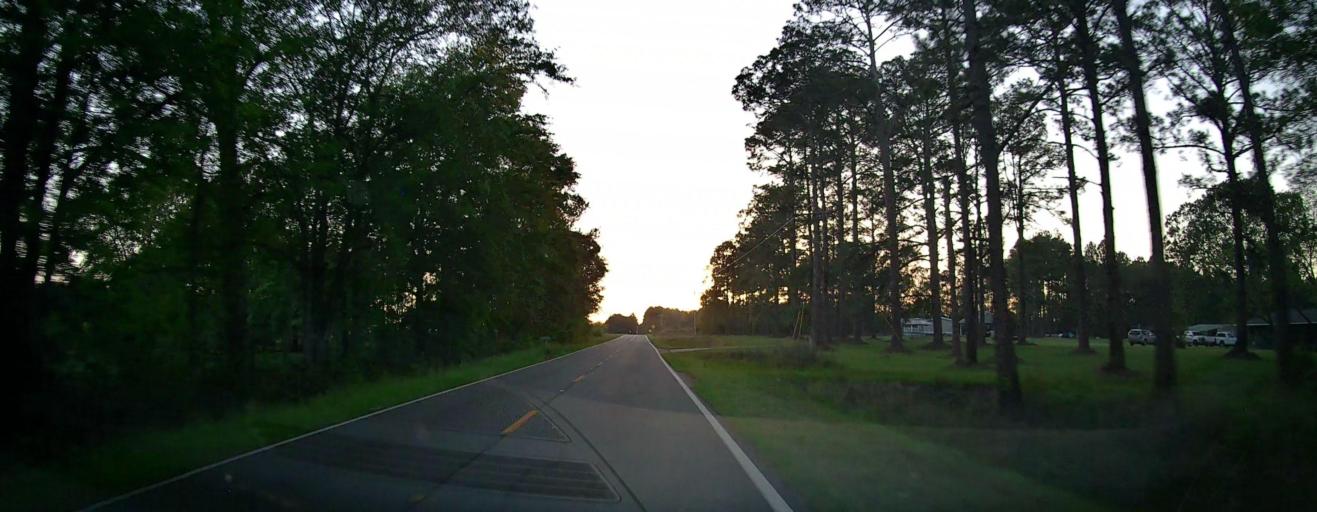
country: US
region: Georgia
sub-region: Wilcox County
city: Rochelle
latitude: 31.7831
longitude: -83.4268
